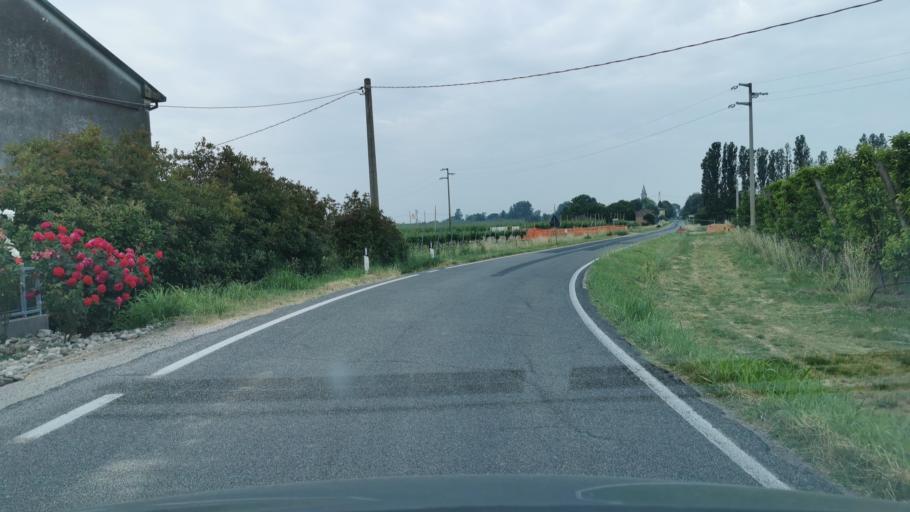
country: IT
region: Emilia-Romagna
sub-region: Provincia di Ravenna
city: Russi
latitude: 44.3838
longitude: 12.0008
